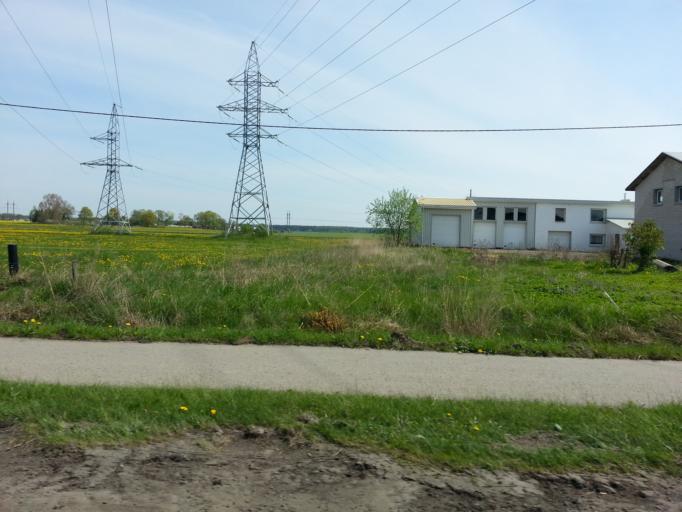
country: LT
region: Panevezys
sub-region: Panevezys City
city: Panevezys
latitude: 55.7648
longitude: 24.3002
